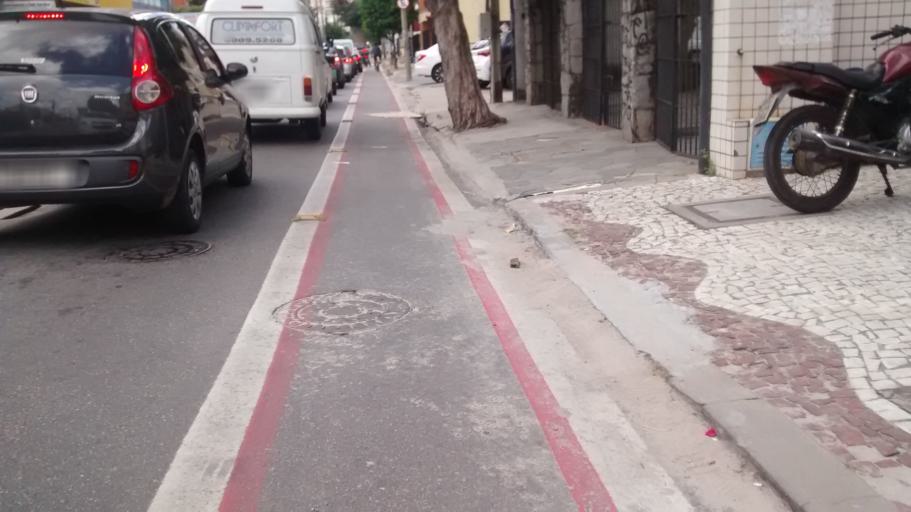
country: BR
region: Ceara
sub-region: Fortaleza
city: Fortaleza
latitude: -3.7350
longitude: -38.5114
